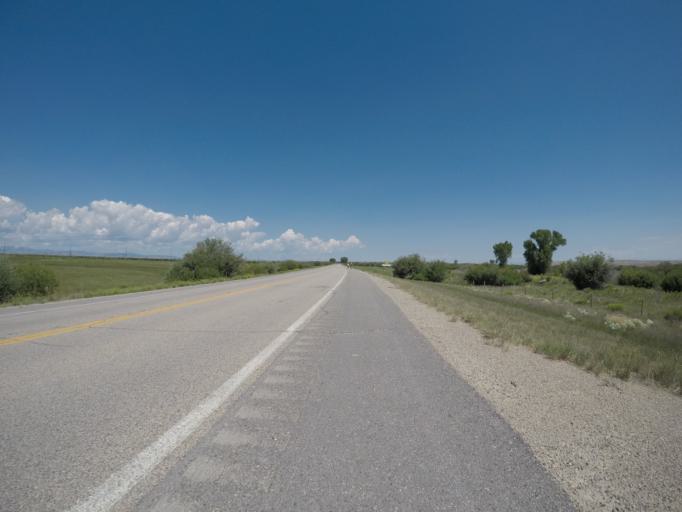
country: US
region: Wyoming
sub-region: Sublette County
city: Marbleton
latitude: 42.5184
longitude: -110.1054
